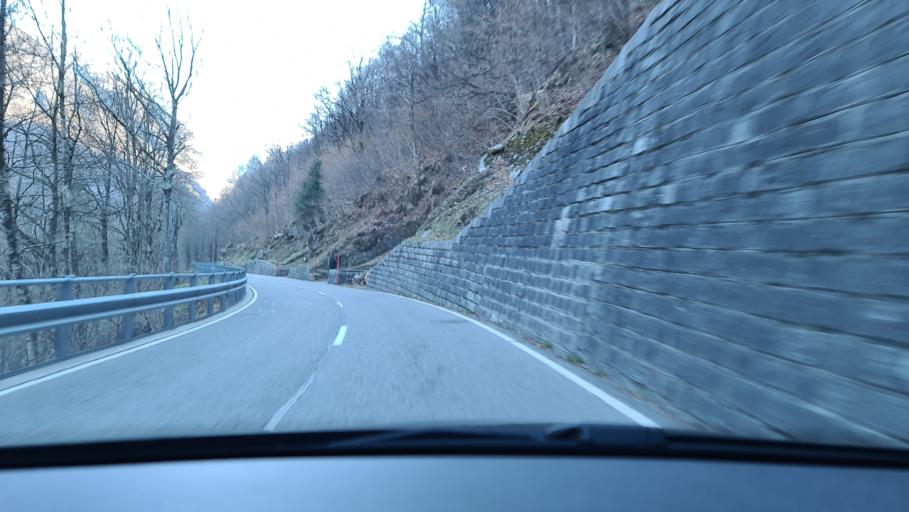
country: CH
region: Ticino
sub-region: Locarno District
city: Lavertezzo
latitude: 46.3281
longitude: 8.8009
